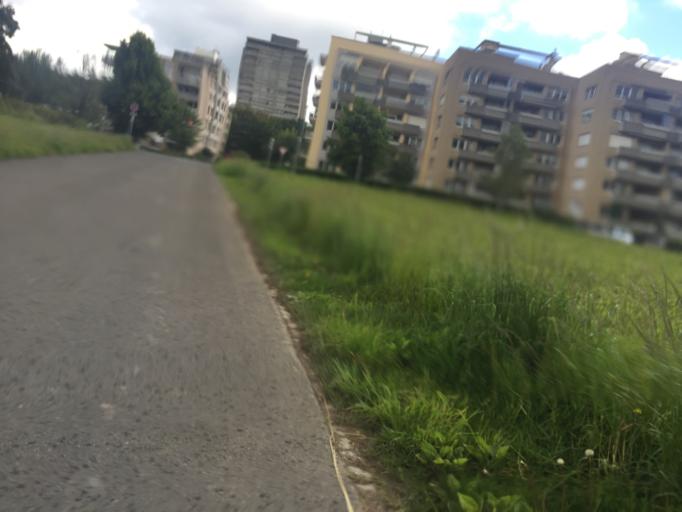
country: CH
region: Bern
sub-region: Bern-Mittelland District
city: Wohlen
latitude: 46.9634
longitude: 7.3771
